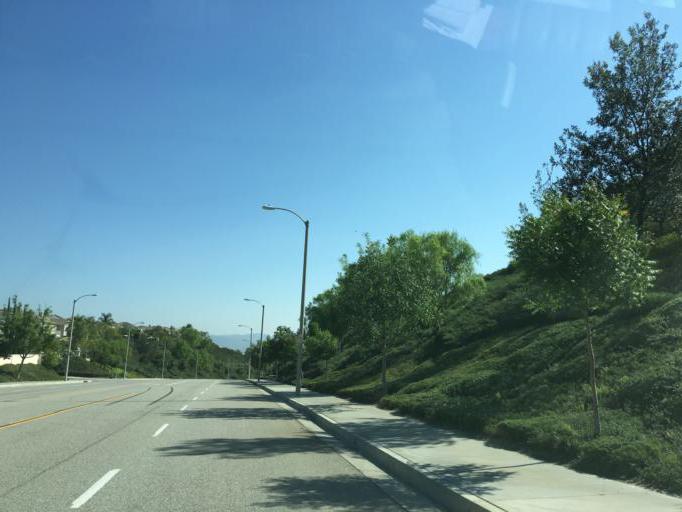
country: US
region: California
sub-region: Los Angeles County
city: Valencia
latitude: 34.3931
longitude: -118.5993
